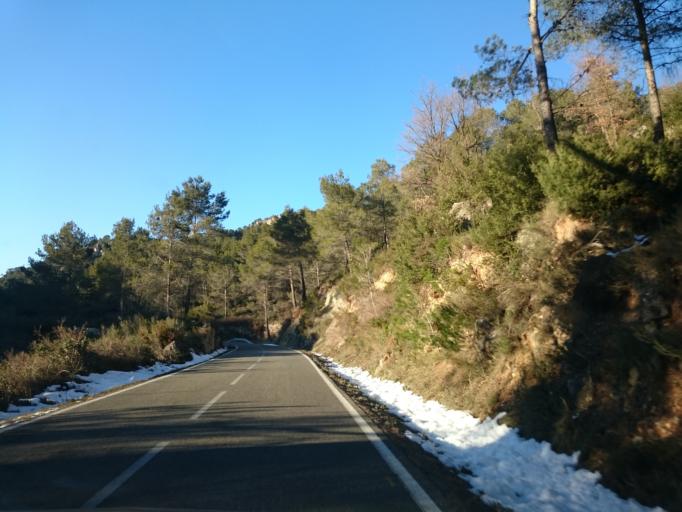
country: ES
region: Catalonia
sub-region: Provincia de Tarragona
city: la Bisbal del Penedes
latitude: 41.3765
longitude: 1.4804
